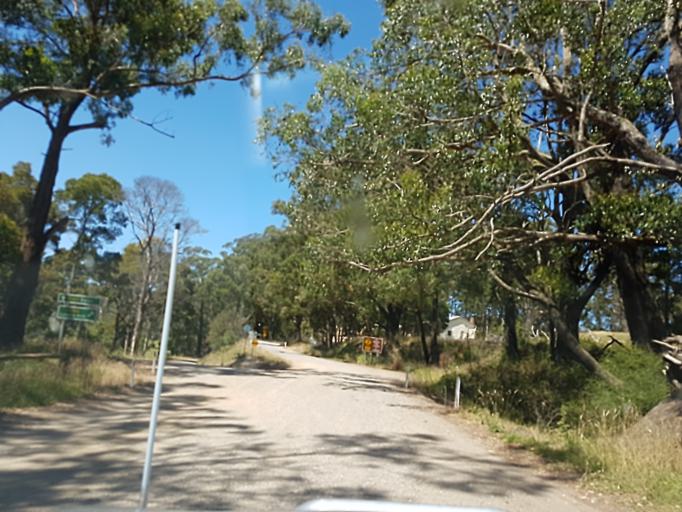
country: AU
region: Victoria
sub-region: Colac-Otway
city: Apollo Bay
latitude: -38.6255
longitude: 143.2761
